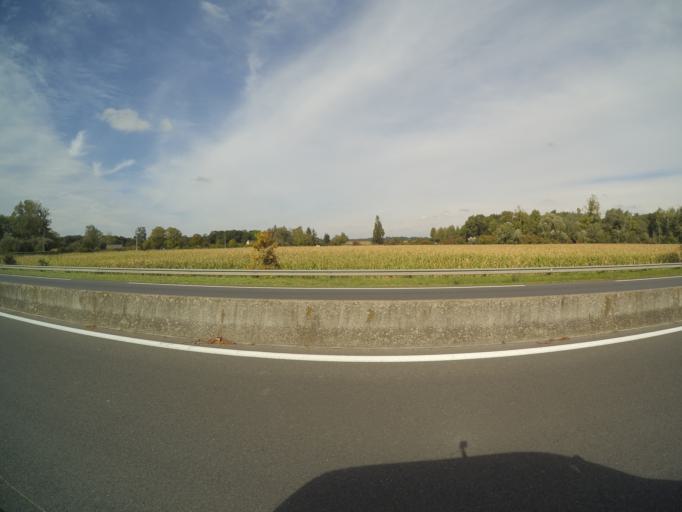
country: FR
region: Pays de la Loire
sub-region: Departement de Maine-et-Loire
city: Distre
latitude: 47.2261
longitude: -0.1395
